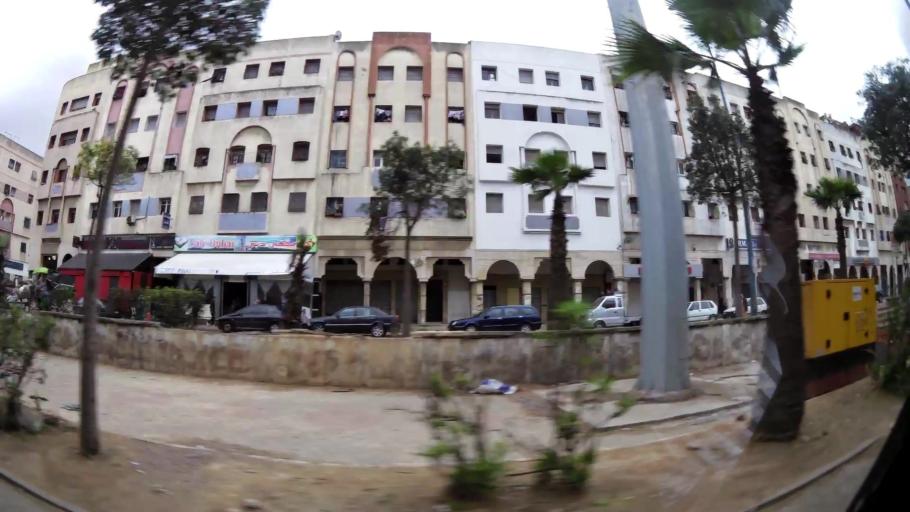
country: MA
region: Grand Casablanca
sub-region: Mediouna
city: Tit Mellil
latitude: 33.5630
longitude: -7.5485
